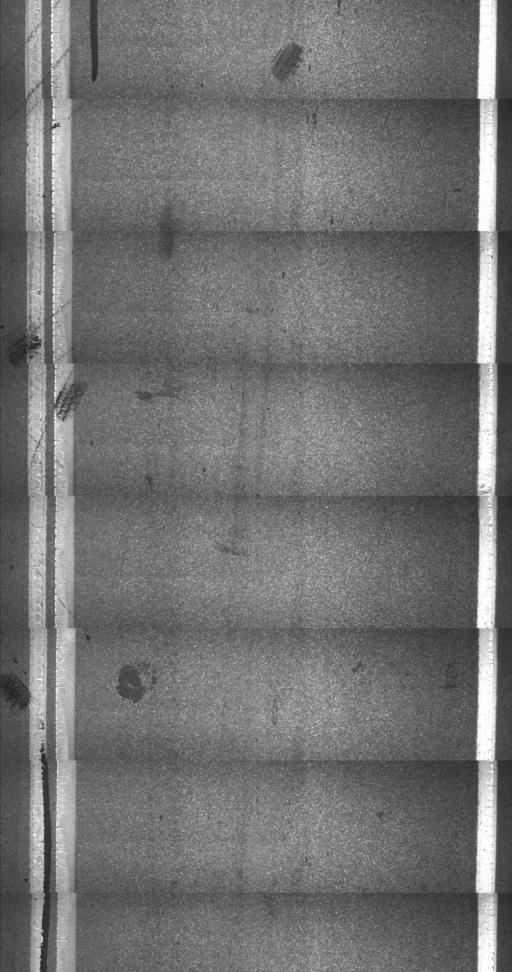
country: US
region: Vermont
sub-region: Rutland County
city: West Rutland
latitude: 43.6086
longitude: -73.0169
